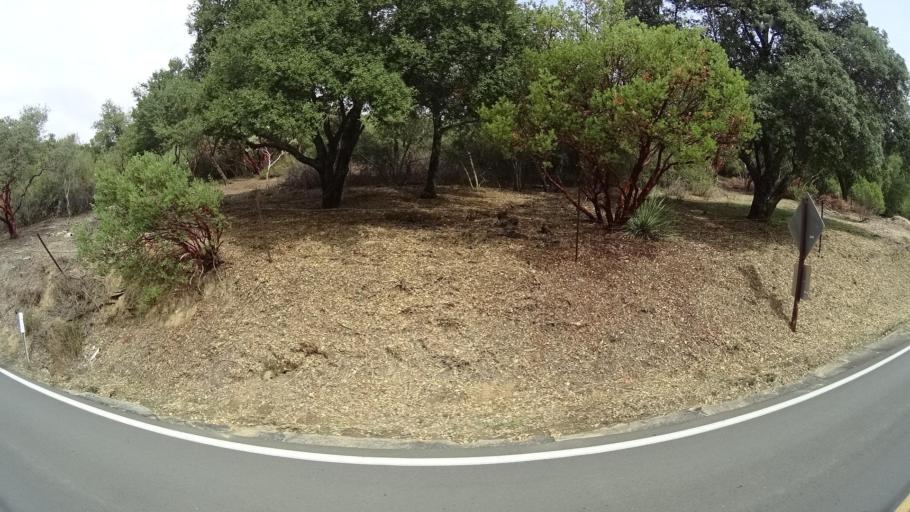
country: US
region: California
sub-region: San Diego County
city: Descanso
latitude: 32.8734
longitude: -116.6347
